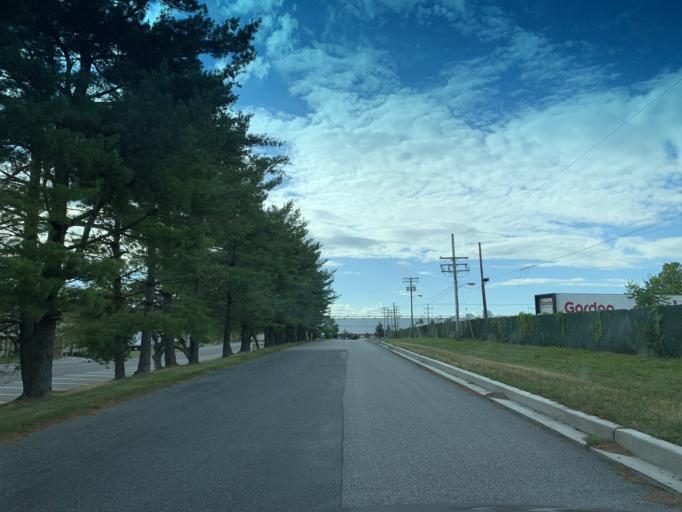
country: US
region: Maryland
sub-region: Harford County
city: Perryman
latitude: 39.4879
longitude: -76.1838
